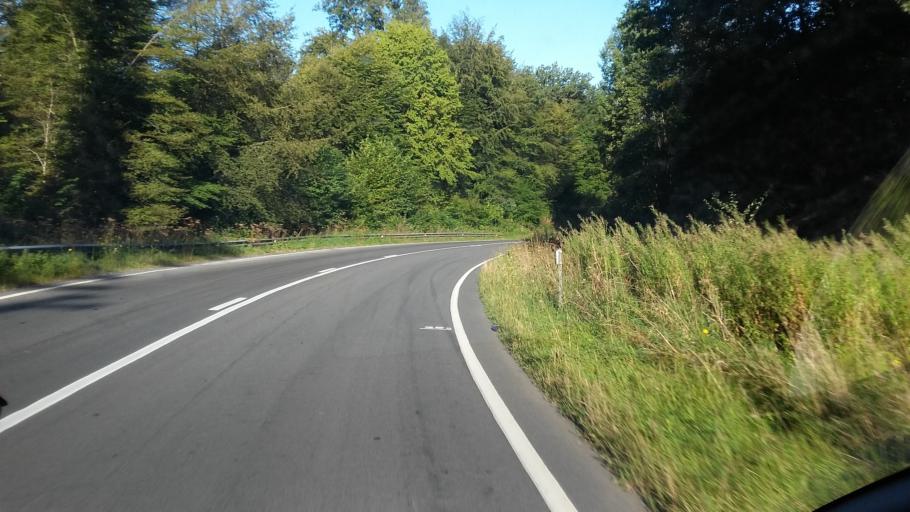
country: BE
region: Wallonia
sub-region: Province du Luxembourg
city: Leglise
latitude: 49.8091
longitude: 5.5103
